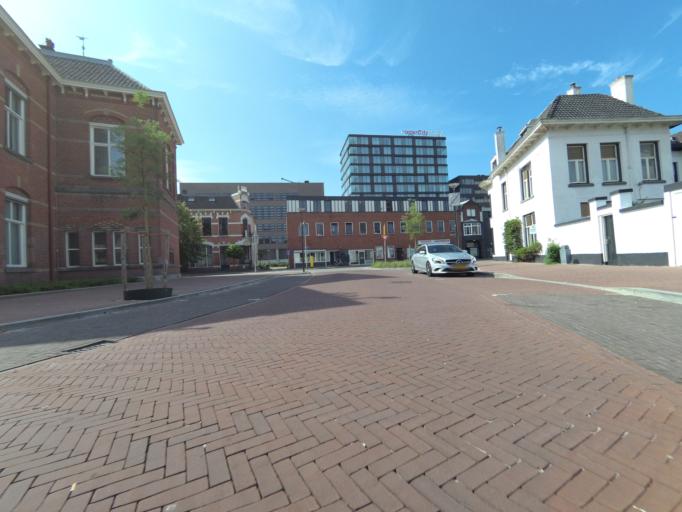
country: NL
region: Overijssel
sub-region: Gemeente Enschede
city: Enschede
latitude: 52.2237
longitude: 6.8942
